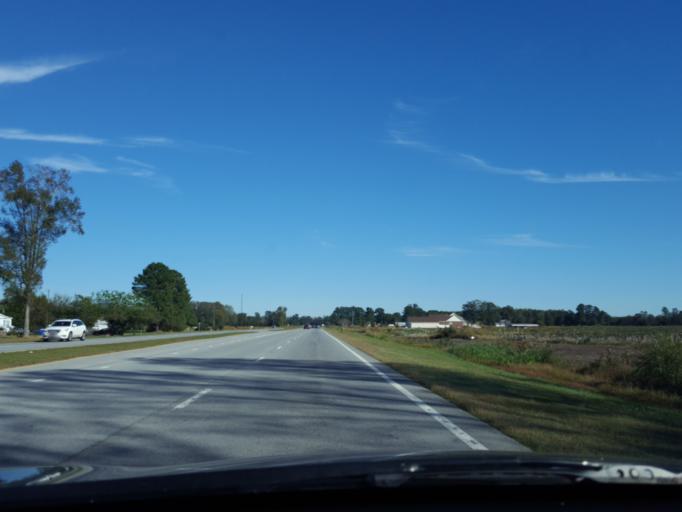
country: US
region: North Carolina
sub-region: Beaufort County
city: Washington
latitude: 35.6261
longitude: -77.1934
